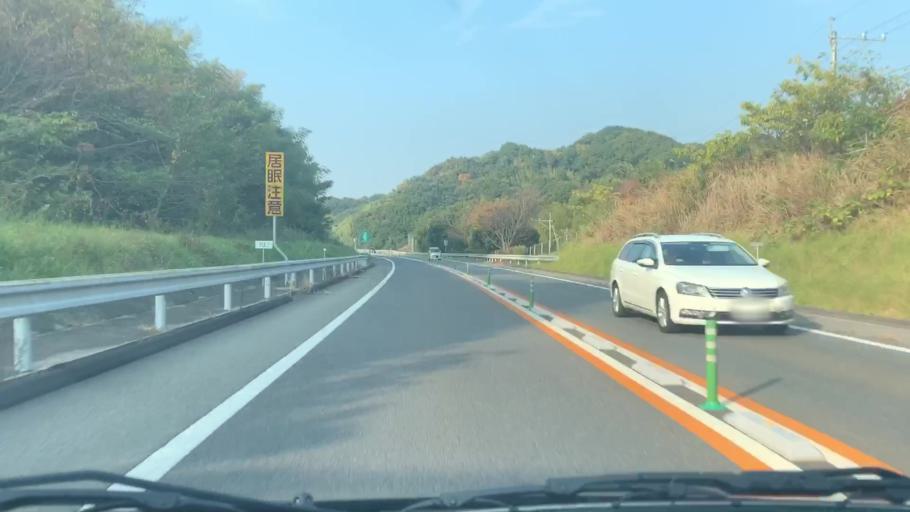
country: JP
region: Nagasaki
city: Sasebo
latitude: 33.1512
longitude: 129.7992
